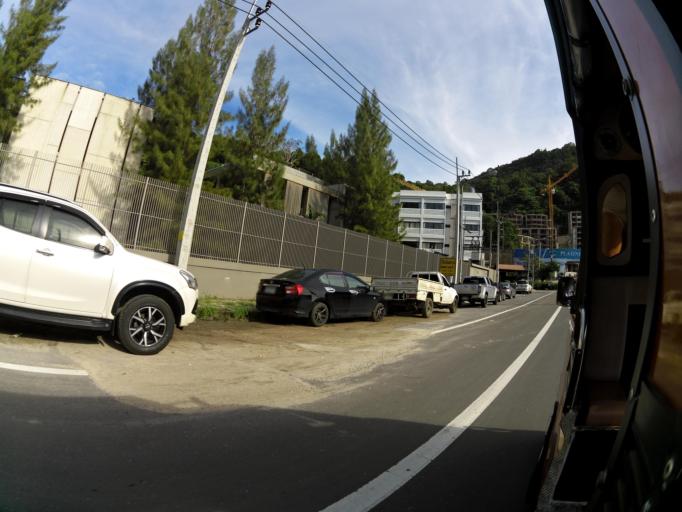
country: TH
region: Phuket
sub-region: Amphoe Kathu
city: Kathu
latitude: 7.9632
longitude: 98.2848
